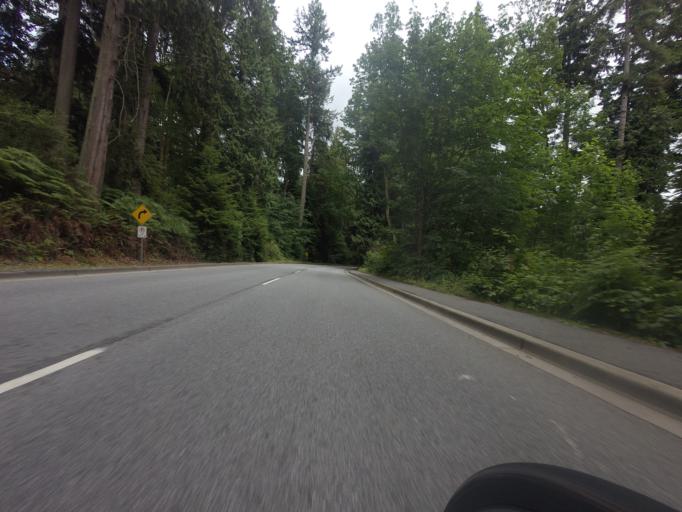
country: CA
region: British Columbia
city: West End
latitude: 49.3034
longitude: -123.1534
